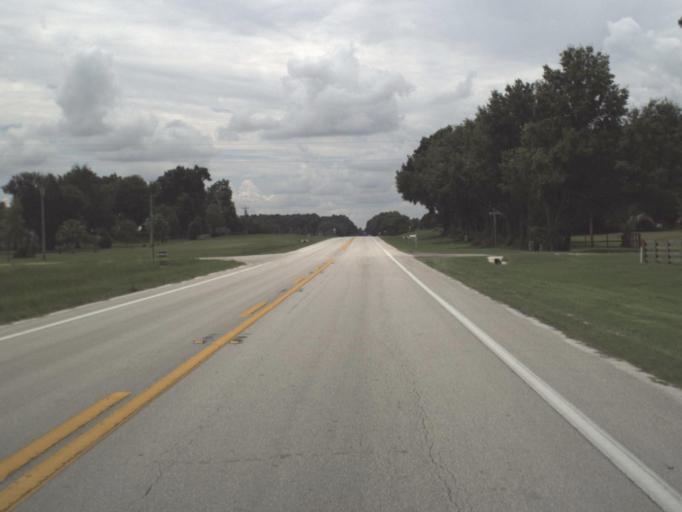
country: US
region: Florida
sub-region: Alachua County
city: High Springs
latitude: 29.7572
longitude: -82.6075
